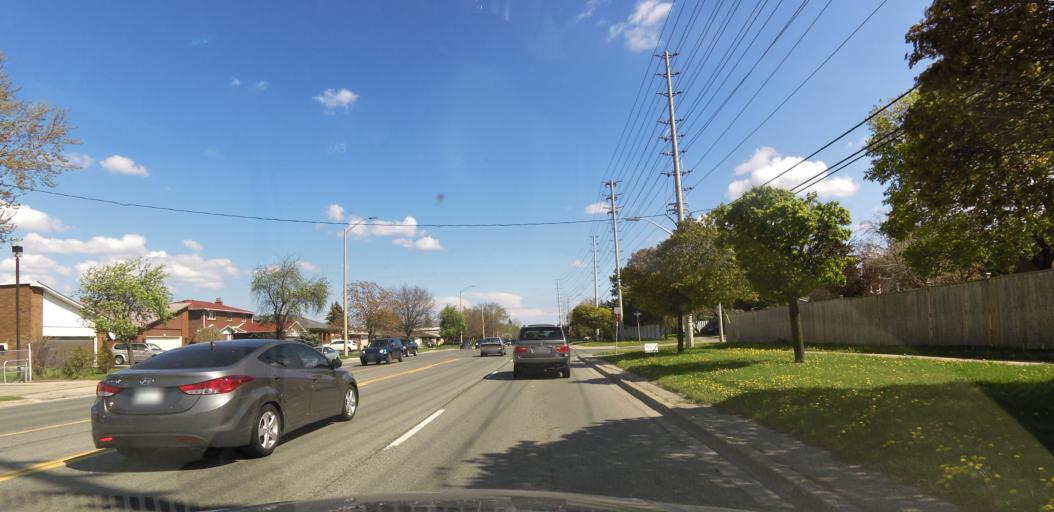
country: CA
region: Ontario
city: Mississauga
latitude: 43.5995
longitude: -79.6071
